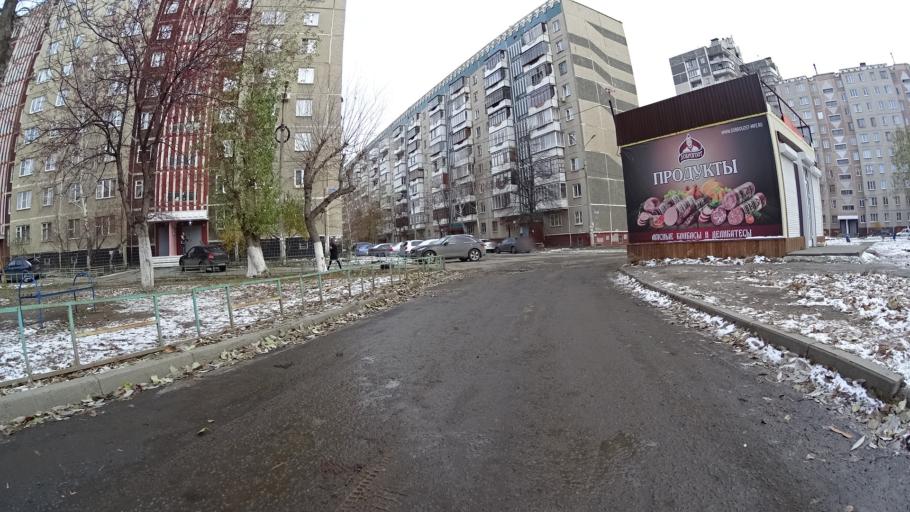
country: RU
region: Chelyabinsk
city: Roshchino
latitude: 55.1877
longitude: 61.2988
